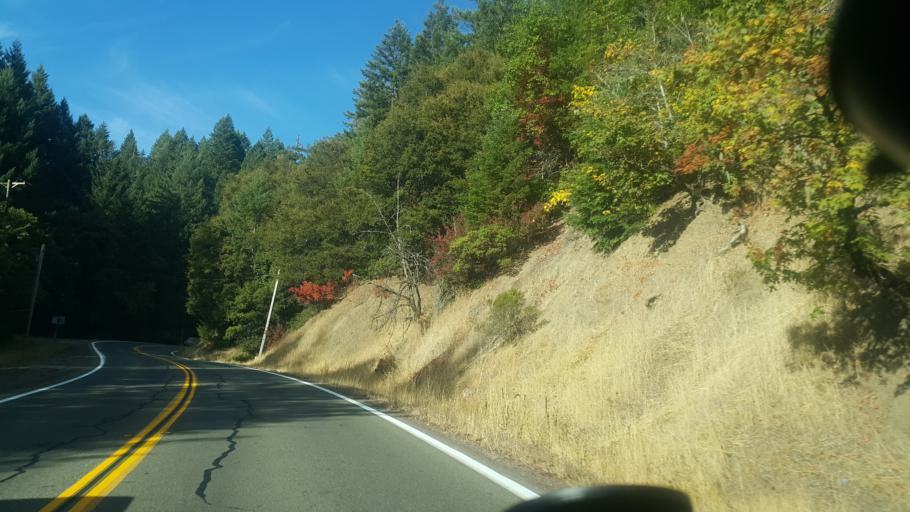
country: US
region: California
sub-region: Mendocino County
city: Brooktrails
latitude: 39.3881
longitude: -123.4345
